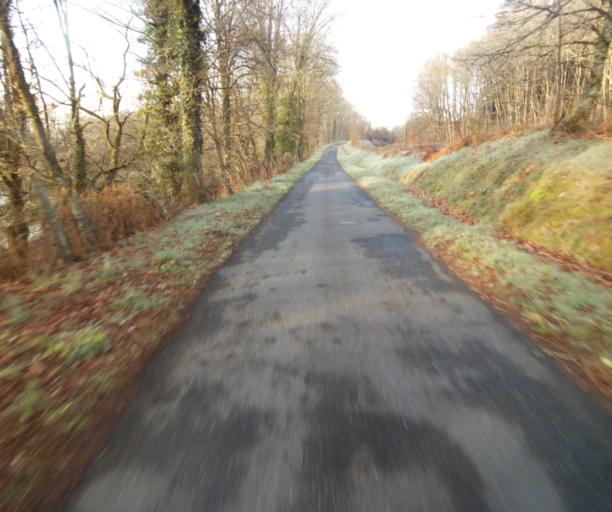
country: FR
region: Limousin
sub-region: Departement de la Correze
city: Correze
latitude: 45.3100
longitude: 1.8570
